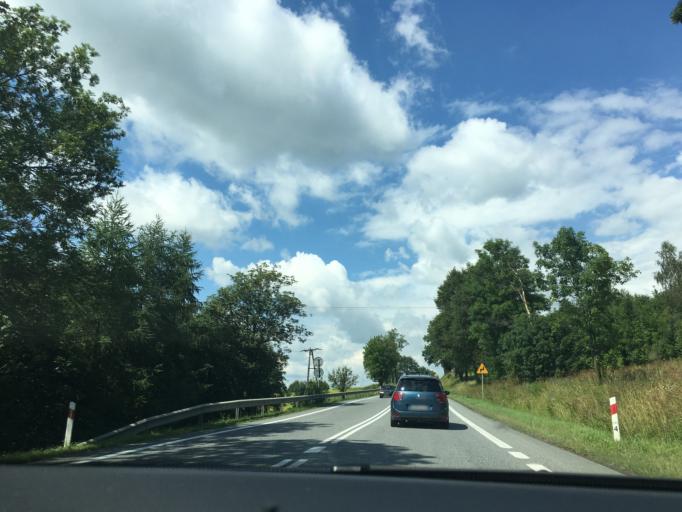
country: PL
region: Subcarpathian Voivodeship
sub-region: Powiat krosnienski
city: Dukla
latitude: 49.5814
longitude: 21.7037
